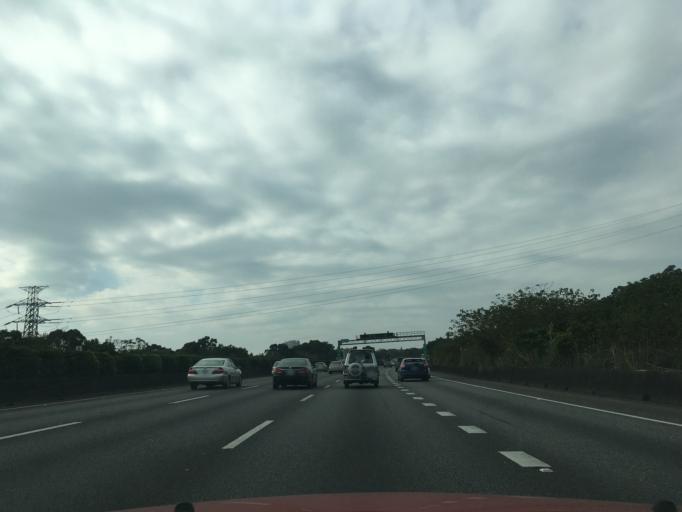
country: TW
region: Taiwan
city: Daxi
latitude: 24.9128
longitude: 121.2929
